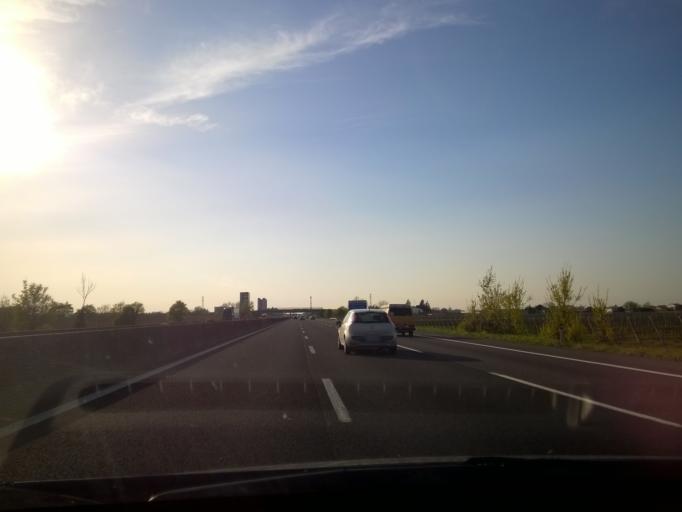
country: IT
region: Emilia-Romagna
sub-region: Provincia di Bologna
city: Imola
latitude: 44.3780
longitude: 11.7497
